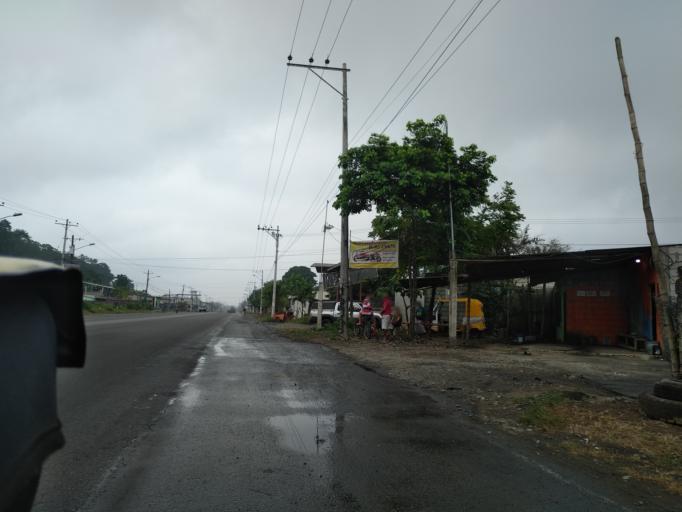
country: EC
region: Cotopaxi
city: La Mana
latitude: -0.9481
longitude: -79.3406
